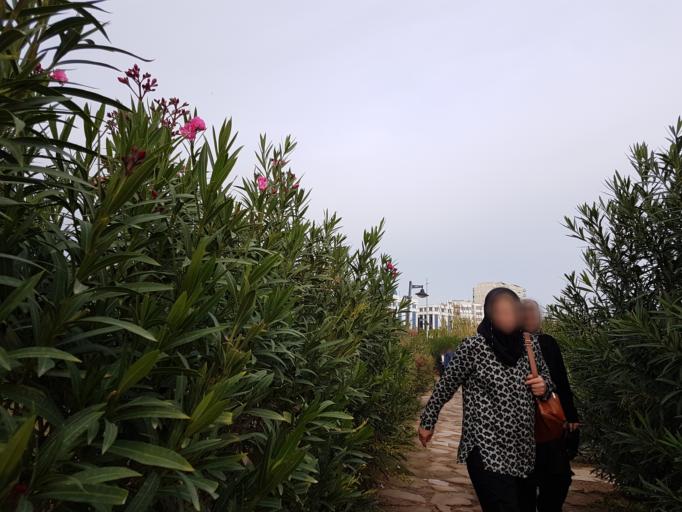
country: TR
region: Antalya
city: Antalya
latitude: 36.8504
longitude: 30.7824
